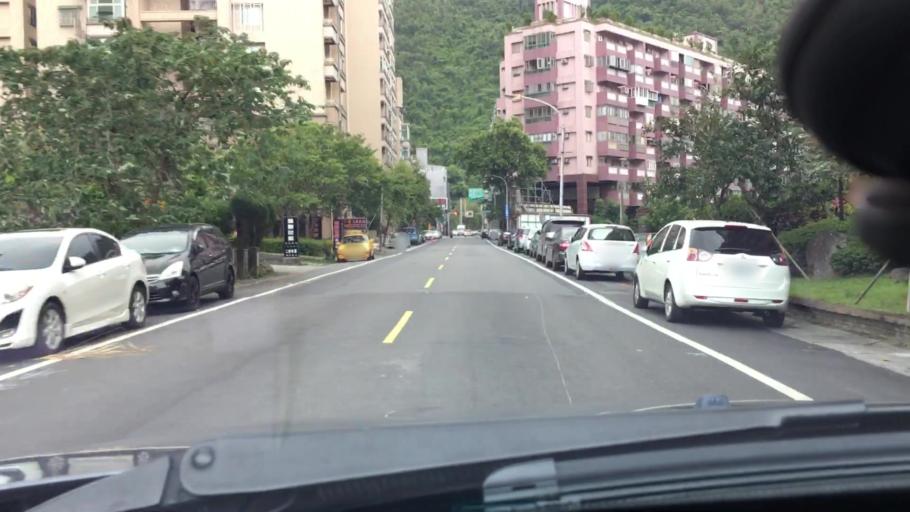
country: TW
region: Taiwan
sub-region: Yilan
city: Yilan
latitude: 24.8242
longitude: 121.7644
